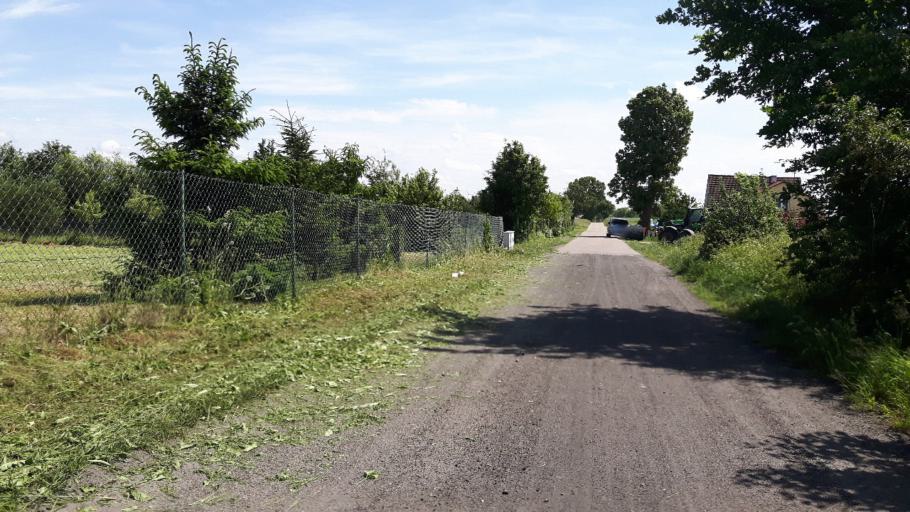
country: PL
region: Pomeranian Voivodeship
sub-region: Powiat wejherowski
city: Gniewino
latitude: 54.7274
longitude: 17.9568
